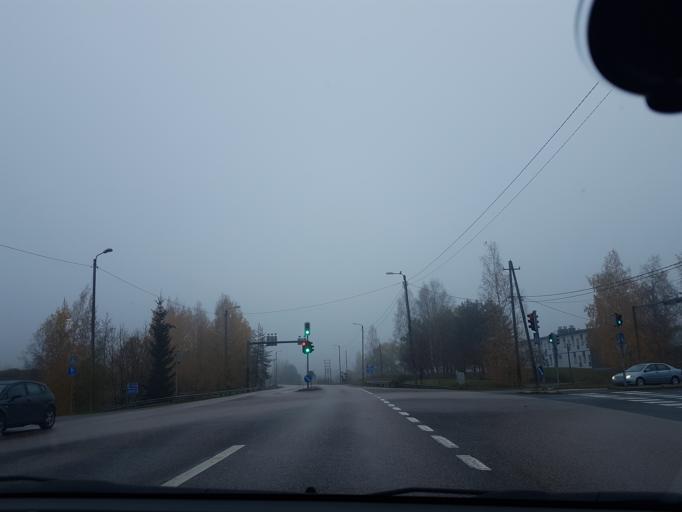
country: FI
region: Uusimaa
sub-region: Helsinki
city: Tuusula
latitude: 60.4144
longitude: 25.0505
